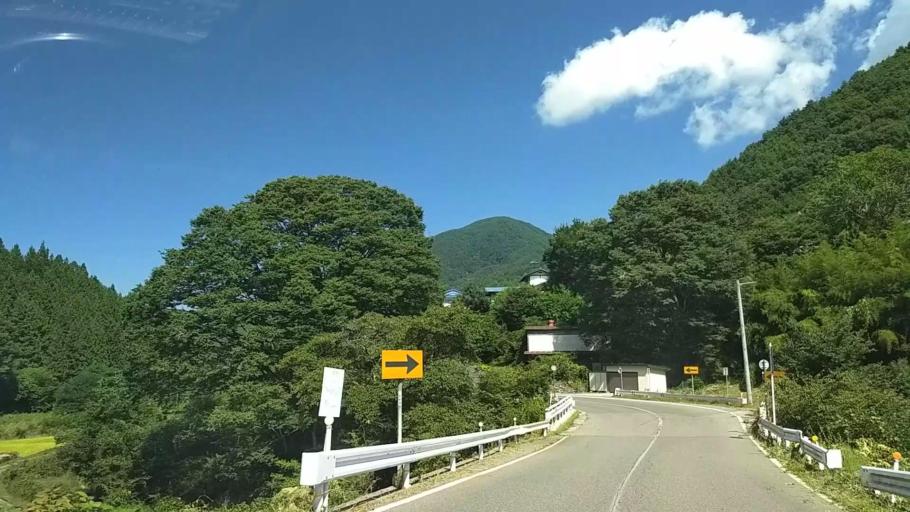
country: JP
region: Nagano
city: Matsumoto
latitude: 36.2120
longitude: 138.0544
